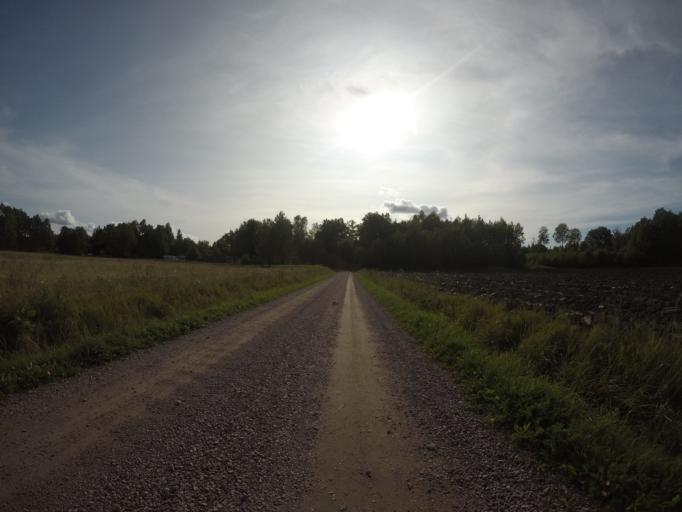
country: SE
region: Soedermanland
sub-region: Eskilstuna Kommun
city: Kvicksund
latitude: 59.5184
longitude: 16.3083
